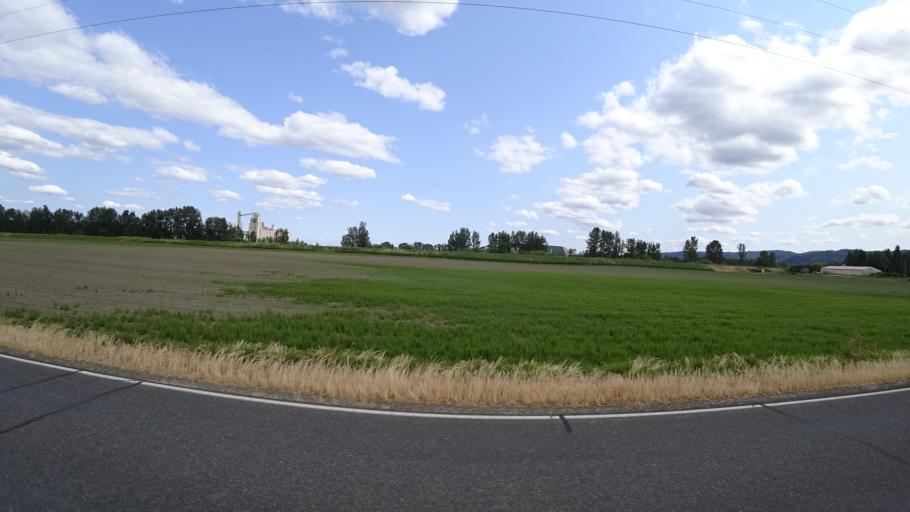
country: US
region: Washington
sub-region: Clark County
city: Felida
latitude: 45.6444
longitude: -122.7820
